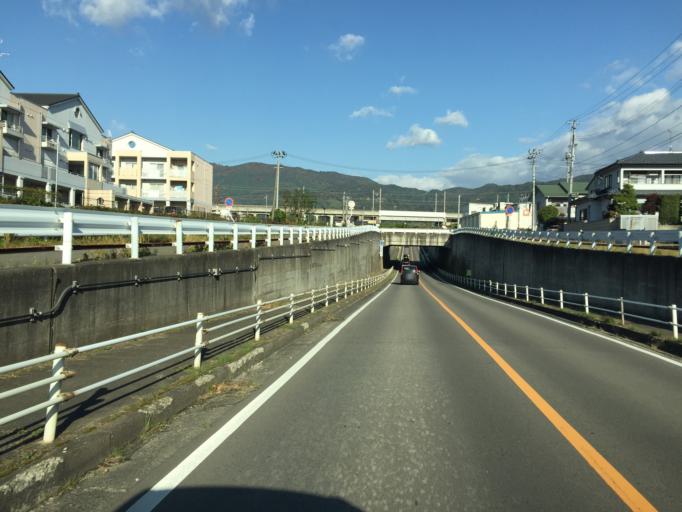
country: JP
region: Fukushima
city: Hobaramachi
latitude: 37.8762
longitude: 140.5376
